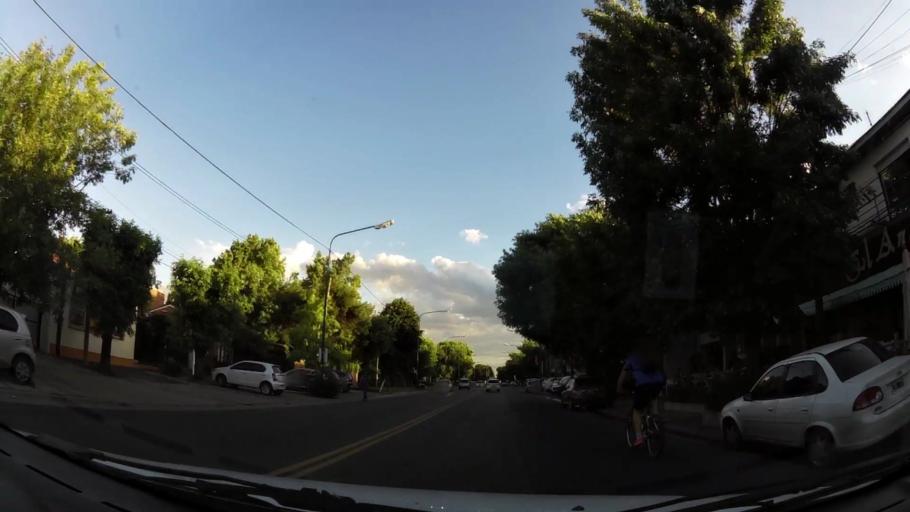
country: AR
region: Buenos Aires
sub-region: Partido de San Isidro
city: San Isidro
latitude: -34.4801
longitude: -58.5286
